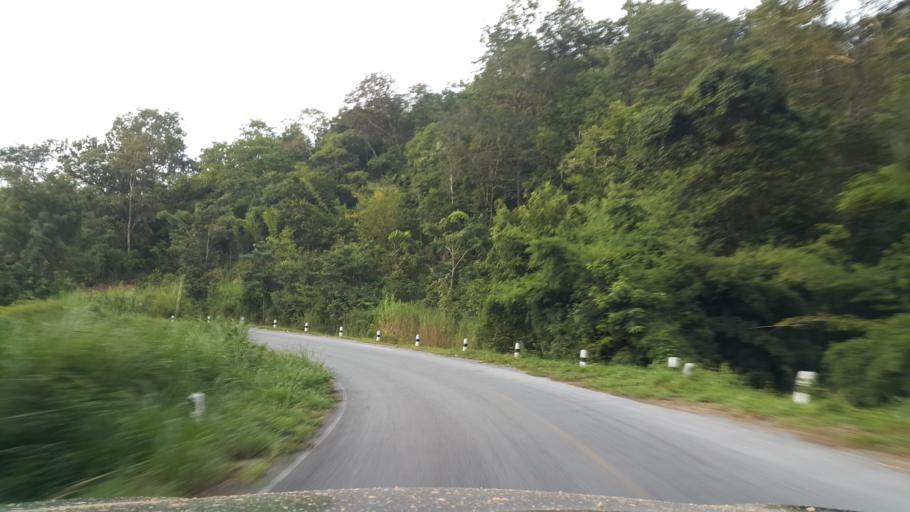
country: TH
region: Mae Hong Son
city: Mae Hi
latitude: 19.2093
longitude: 98.4328
